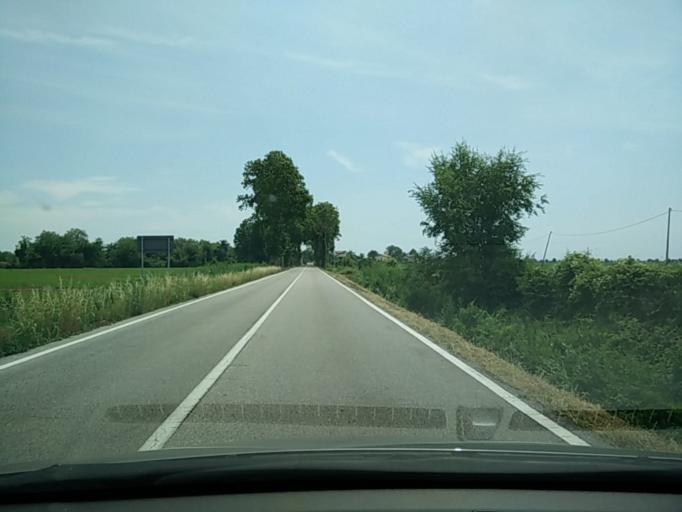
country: IT
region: Veneto
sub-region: Provincia di Venezia
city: Quarto d'Altino
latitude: 45.5634
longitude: 12.4150
